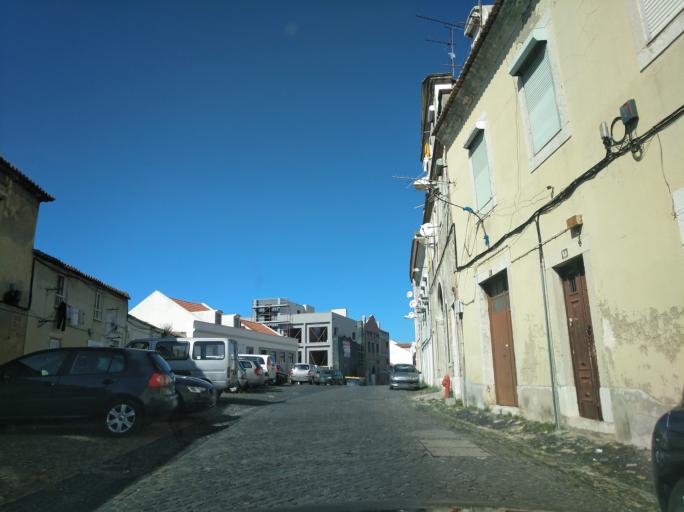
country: PT
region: Lisbon
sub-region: Lisbon
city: Lisbon
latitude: 38.7393
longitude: -9.1066
